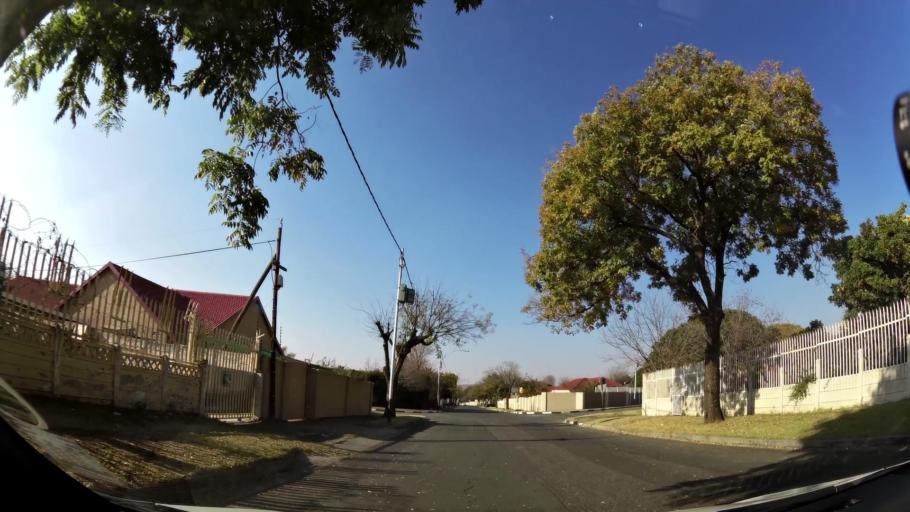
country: ZA
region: Gauteng
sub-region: City of Johannesburg Metropolitan Municipality
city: Johannesburg
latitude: -26.2431
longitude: 28.0108
